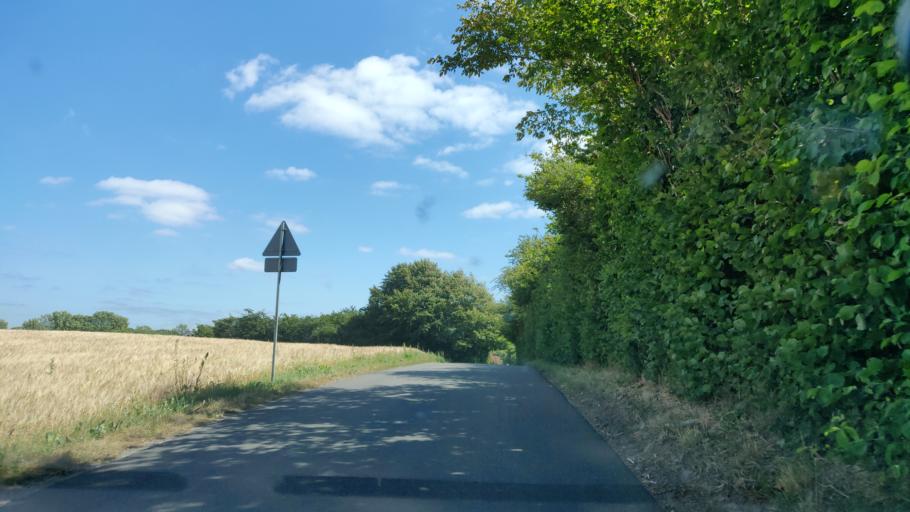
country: DK
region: South Denmark
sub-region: Kolding Kommune
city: Kolding
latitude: 55.5439
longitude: 9.5104
